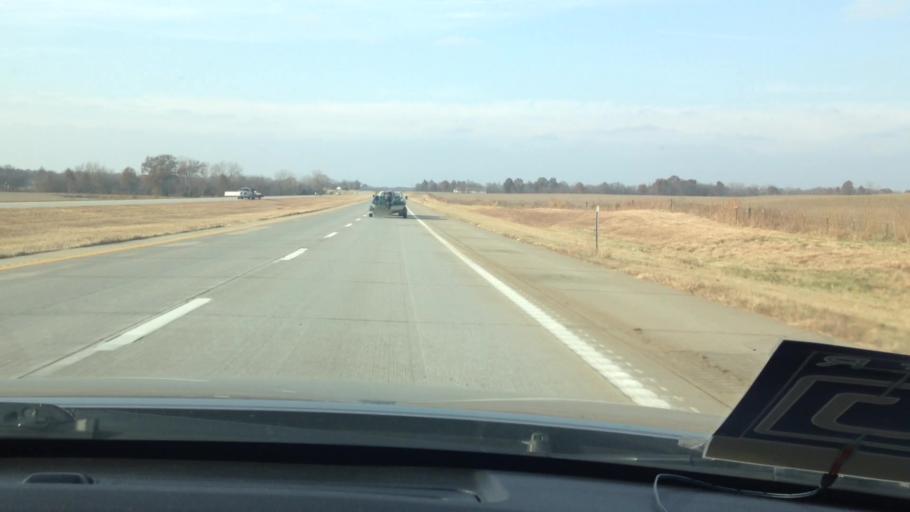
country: US
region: Missouri
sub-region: Henry County
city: Clinton
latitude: 38.4481
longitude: -93.9579
